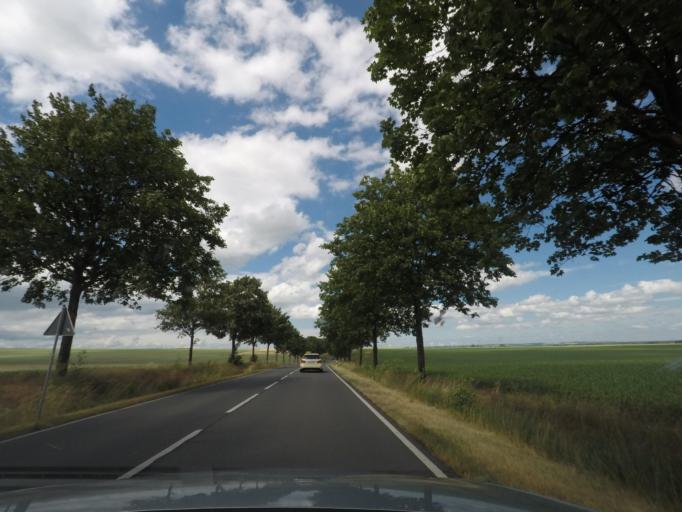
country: DE
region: Saxony-Anhalt
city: Gross Quenstedt
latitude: 51.9424
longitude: 11.1216
